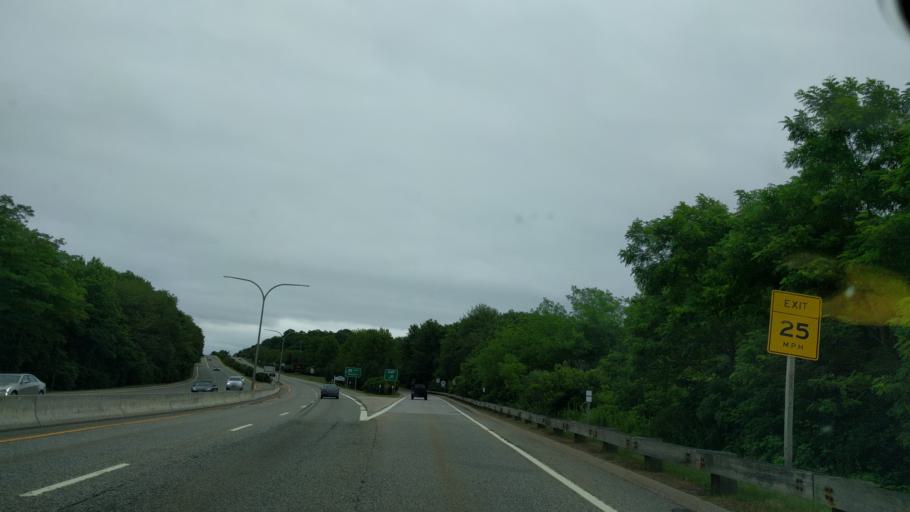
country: US
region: Rhode Island
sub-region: Newport County
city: Jamestown
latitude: 41.5260
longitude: -71.3893
